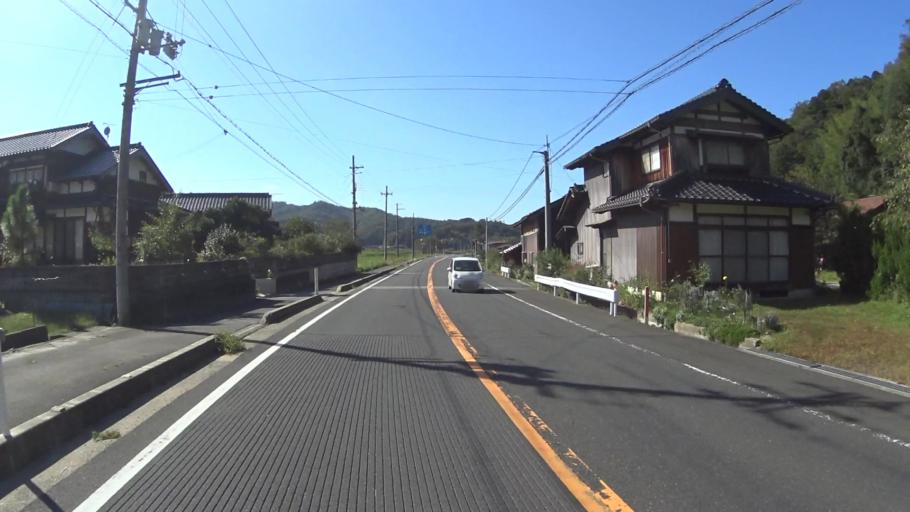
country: JP
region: Hyogo
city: Toyooka
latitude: 35.5728
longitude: 134.9828
